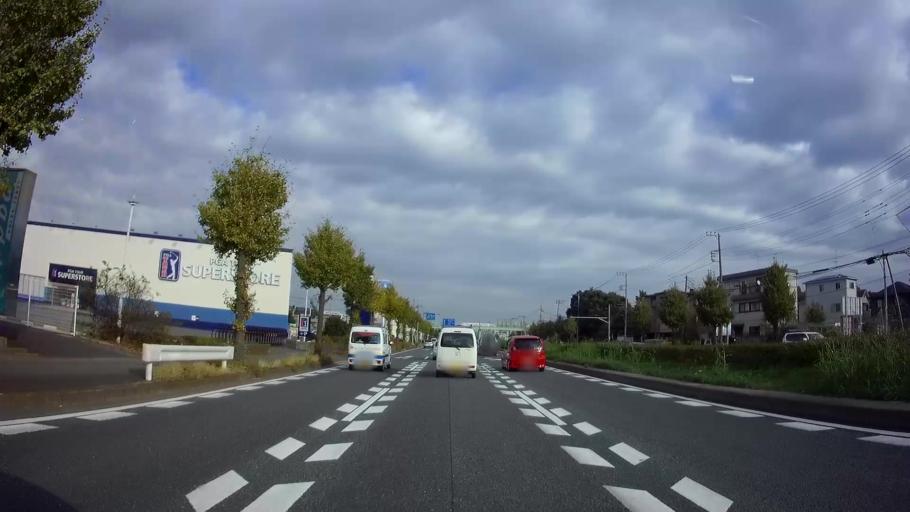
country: JP
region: Saitama
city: Yono
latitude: 35.9130
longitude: 139.5934
